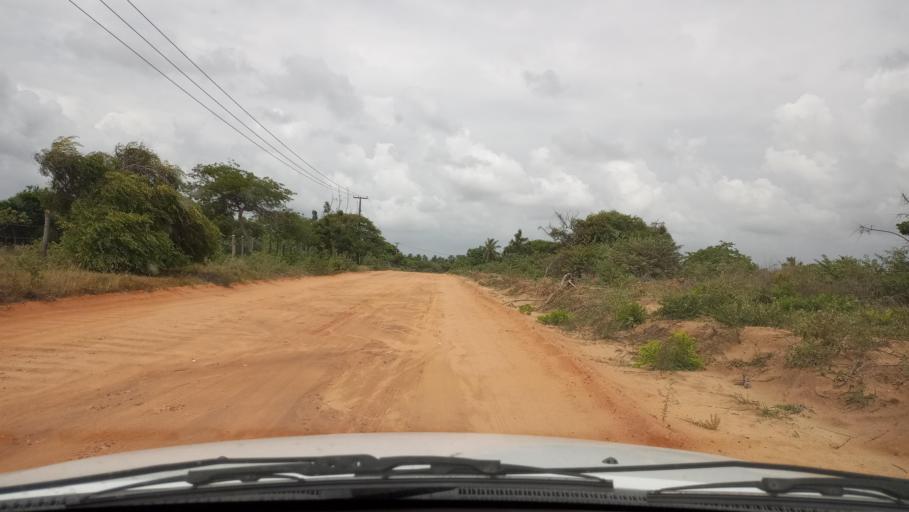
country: BR
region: Rio Grande do Norte
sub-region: Maxaranguape
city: Sao Miguel
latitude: -5.4841
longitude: -35.3092
